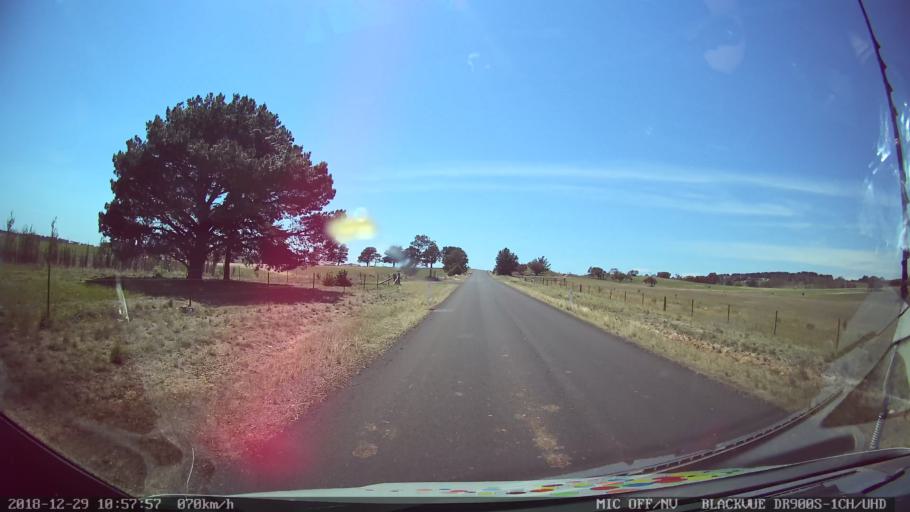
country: AU
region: New South Wales
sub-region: Palerang
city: Bungendore
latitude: -35.1381
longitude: 149.5538
